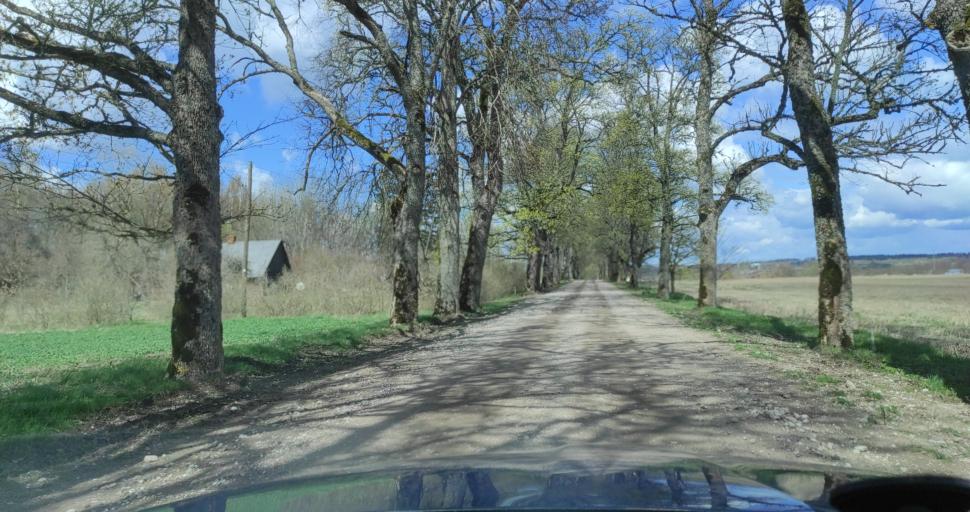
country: LV
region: Kuldigas Rajons
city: Kuldiga
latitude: 56.8572
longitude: 21.8134
